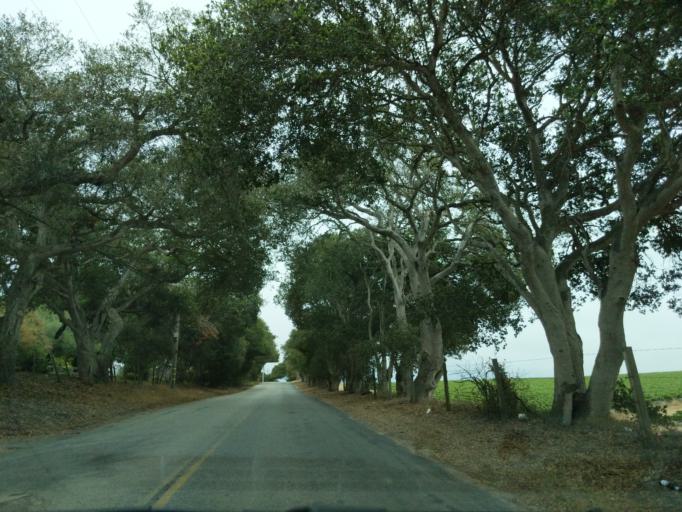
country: US
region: California
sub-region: Monterey County
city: Prunedale
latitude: 36.7887
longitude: -121.6927
